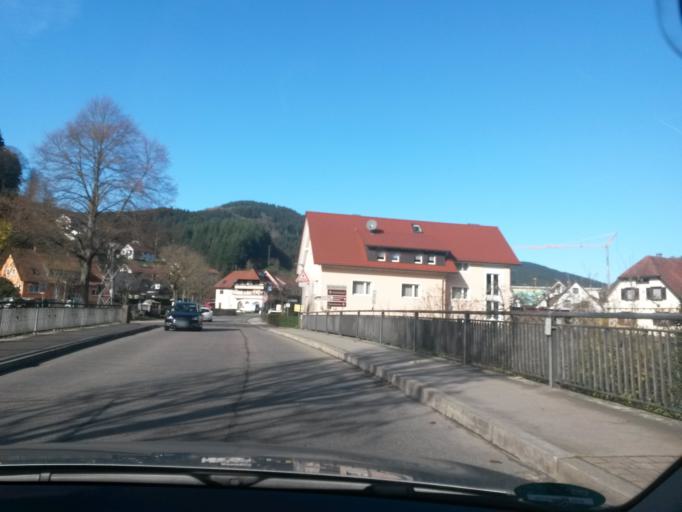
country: DE
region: Baden-Wuerttemberg
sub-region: Freiburg Region
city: Oberwolfach
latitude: 48.3142
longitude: 8.2186
